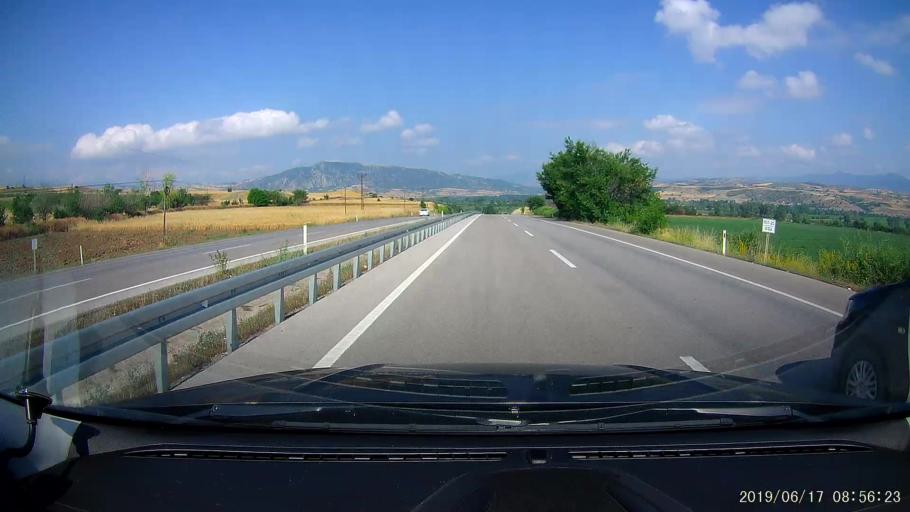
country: TR
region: Amasya
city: Esencay
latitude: 40.7340
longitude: 36.4227
